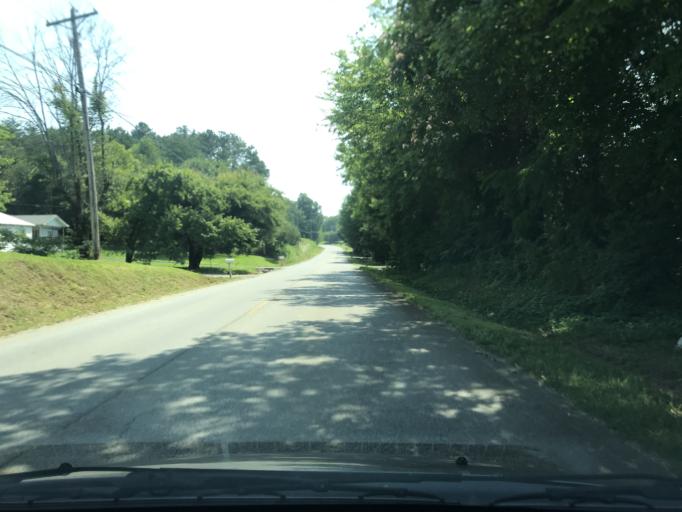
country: US
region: Tennessee
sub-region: Loudon County
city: Lenoir City
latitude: 35.8326
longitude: -84.3071
